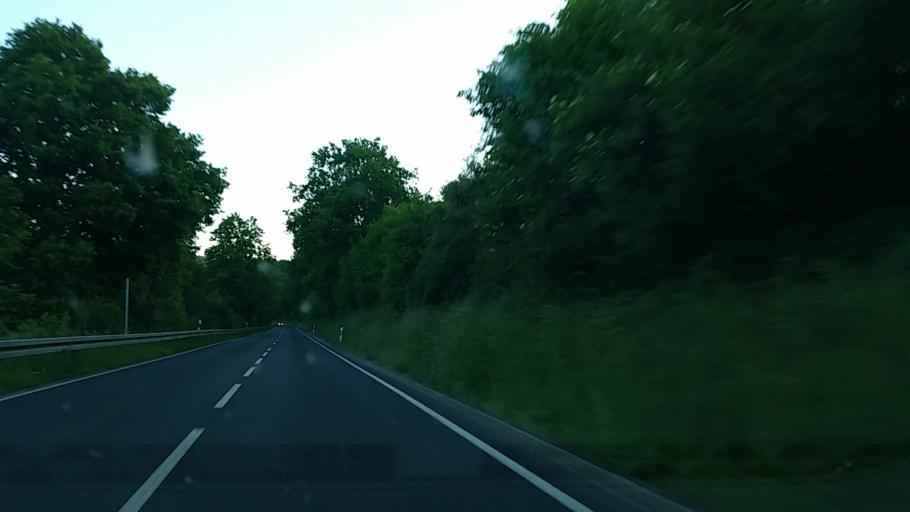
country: DE
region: Bavaria
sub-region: Regierungsbezirk Unterfranken
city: Obersinn
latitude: 50.2447
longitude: 9.6053
